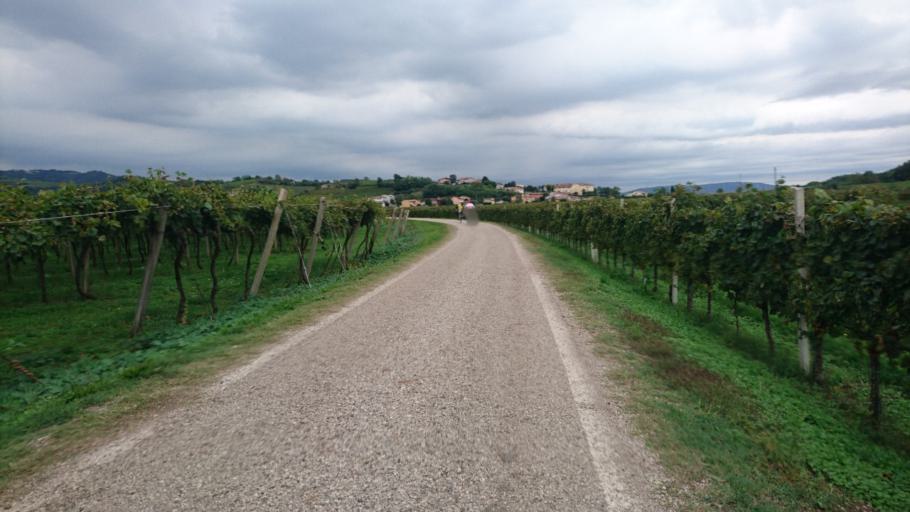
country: IT
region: Veneto
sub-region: Provincia di Vicenza
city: Gambellara
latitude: 45.4390
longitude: 11.3523
